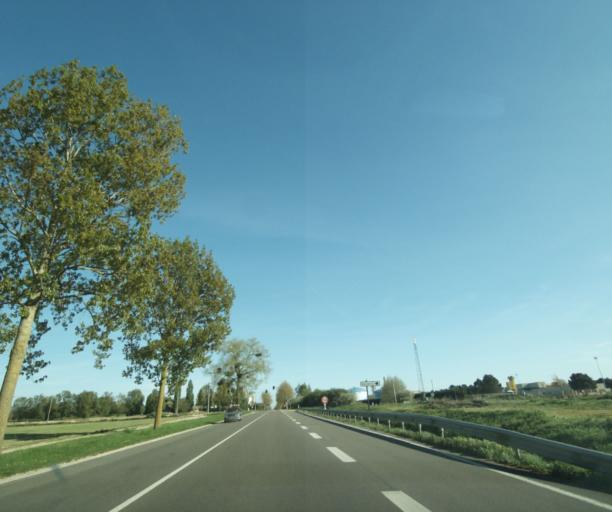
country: FR
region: Ile-de-France
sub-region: Departement de Seine-et-Marne
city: Nangis
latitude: 48.5682
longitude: 3.0043
